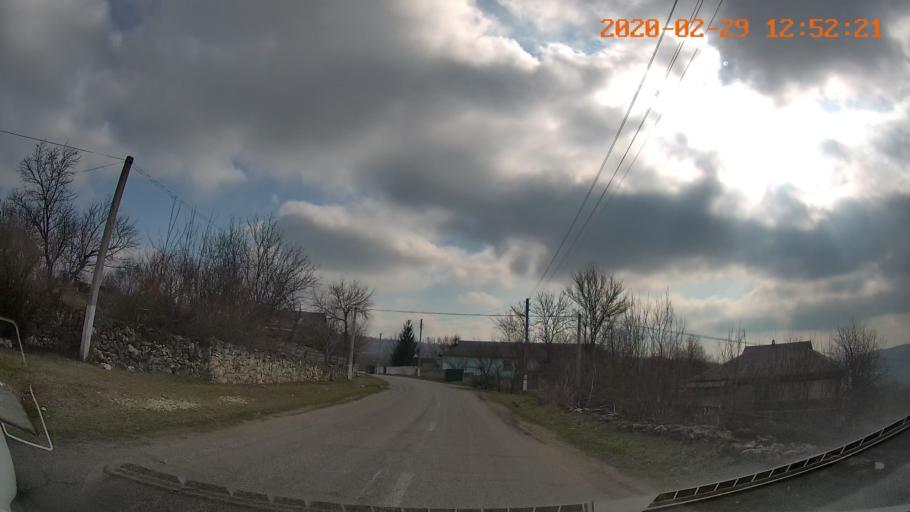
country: MD
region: Telenesti
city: Camenca
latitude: 48.1121
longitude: 28.7329
